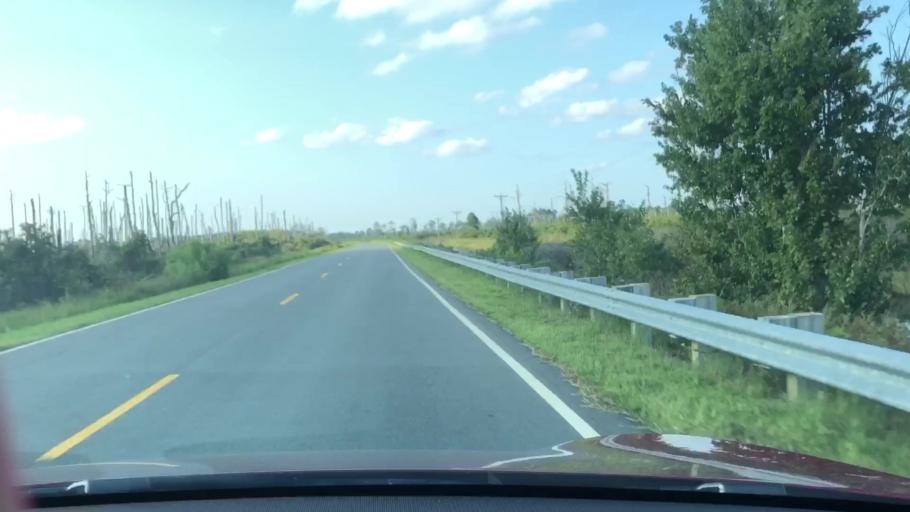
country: US
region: North Carolina
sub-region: Dare County
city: Wanchese
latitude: 35.6572
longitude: -75.7772
